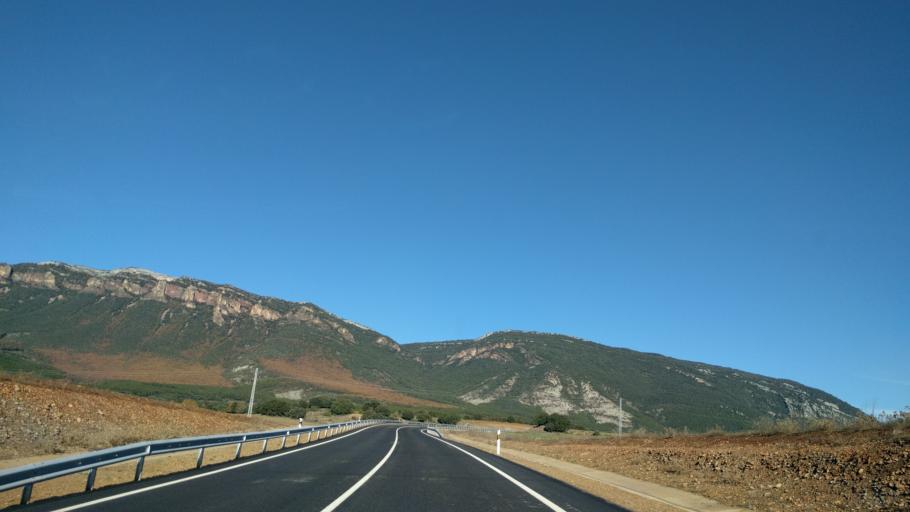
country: ES
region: Aragon
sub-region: Provincia de Zaragoza
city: Siguees
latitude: 42.6152
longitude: -1.0400
